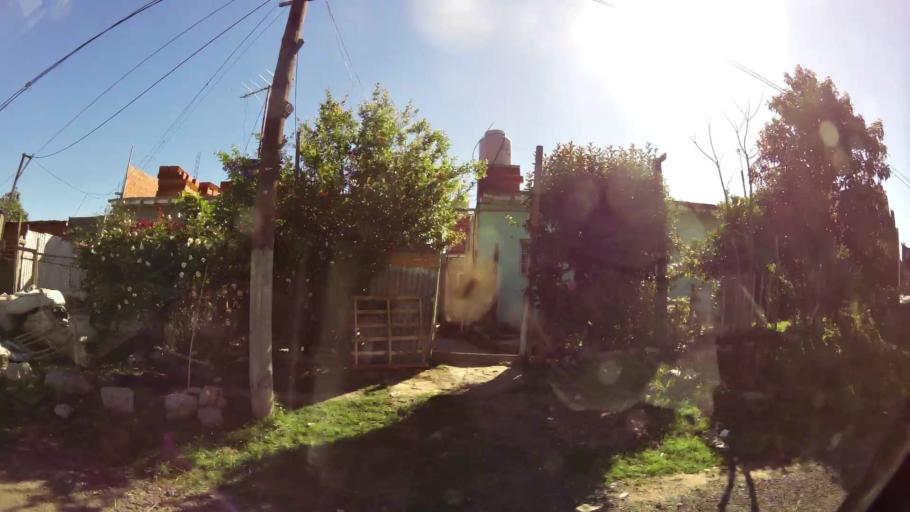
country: AR
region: Buenos Aires
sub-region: Partido de Quilmes
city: Quilmes
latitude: -34.7590
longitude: -58.3093
